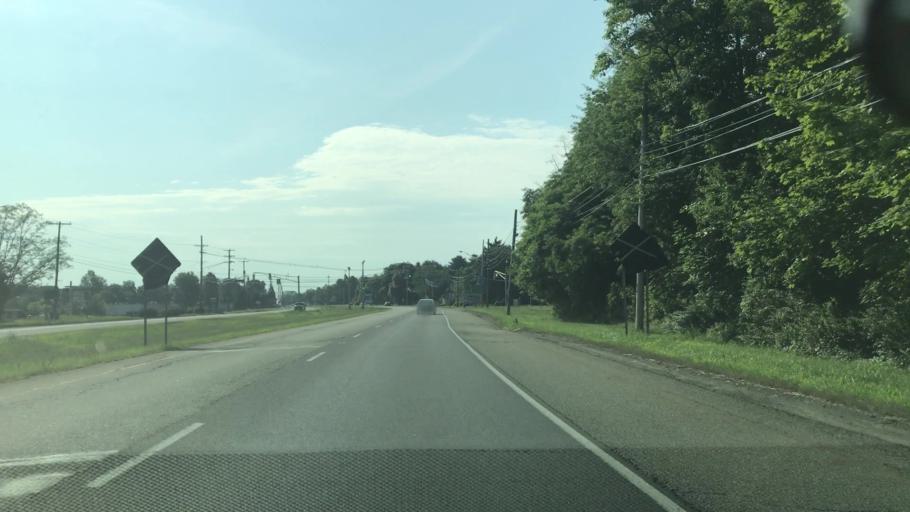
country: US
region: New Jersey
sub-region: Hunterdon County
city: Whitehouse Station
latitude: 40.6106
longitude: -74.7166
